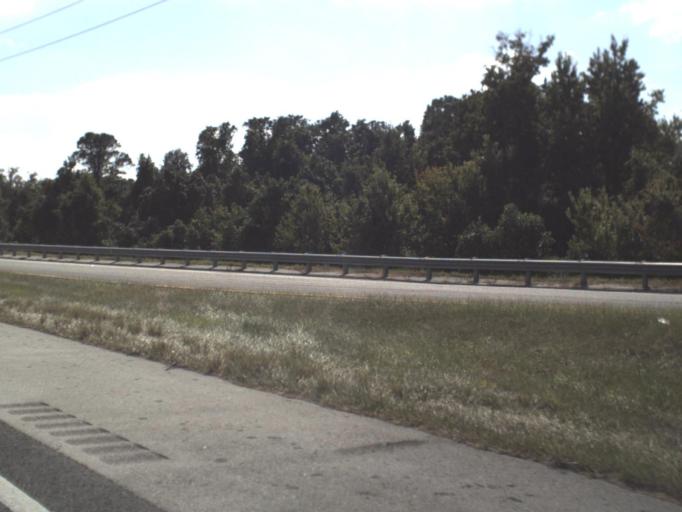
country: US
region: Florida
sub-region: Polk County
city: Citrus Ridge
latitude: 28.2930
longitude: -81.6011
